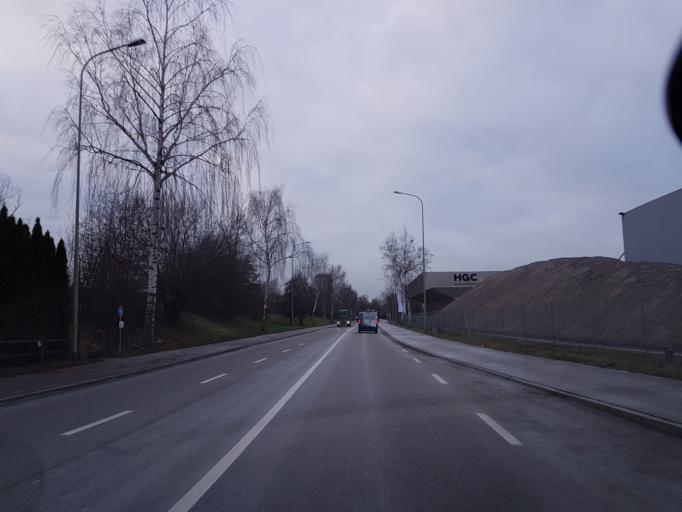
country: CH
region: Zurich
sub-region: Bezirk Dietikon
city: Dietikon / Hofacker
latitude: 47.4038
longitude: 8.4162
